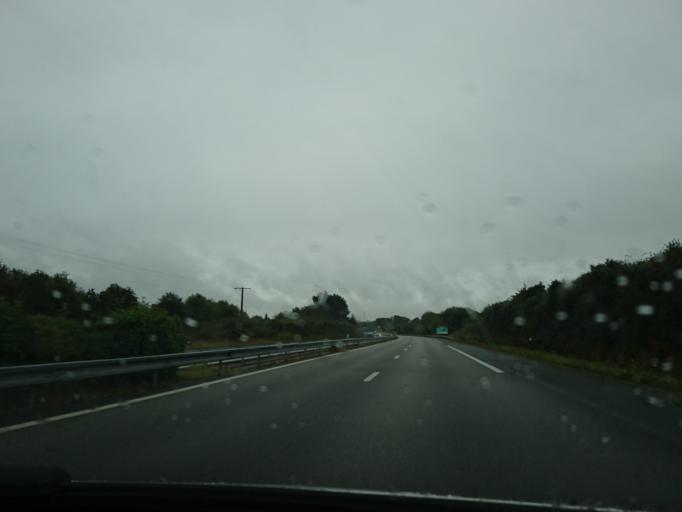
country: FR
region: Brittany
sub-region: Departement du Morbihan
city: Surzur
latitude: 47.6070
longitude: -2.6057
